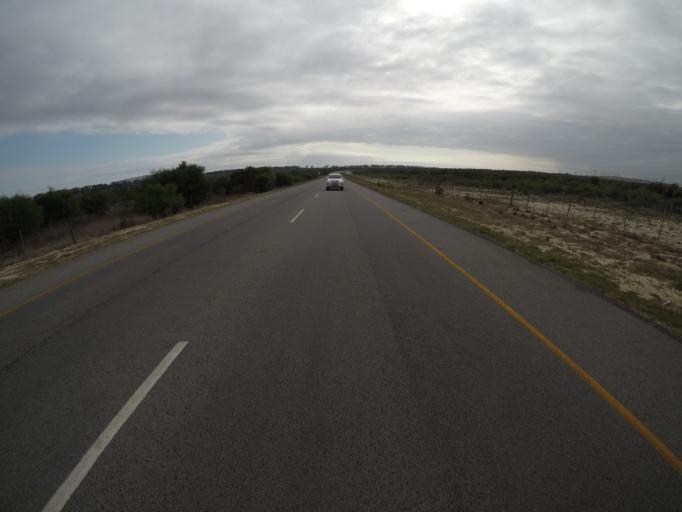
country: ZA
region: Western Cape
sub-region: City of Cape Town
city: Sunset Beach
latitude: -33.7248
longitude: 18.5279
